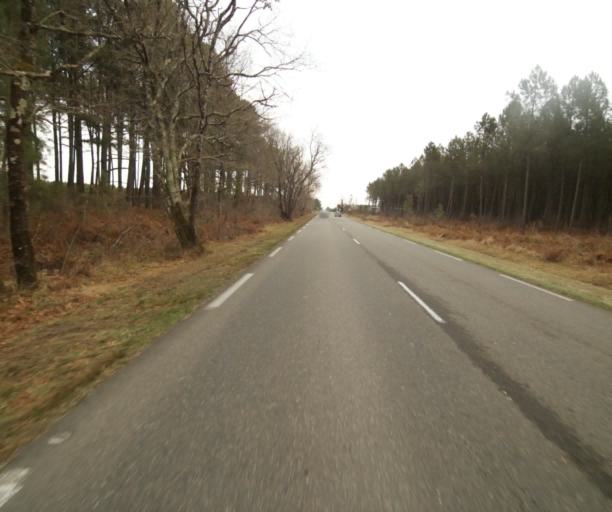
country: FR
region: Aquitaine
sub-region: Departement des Landes
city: Gabarret
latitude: 44.0748
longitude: -0.0430
